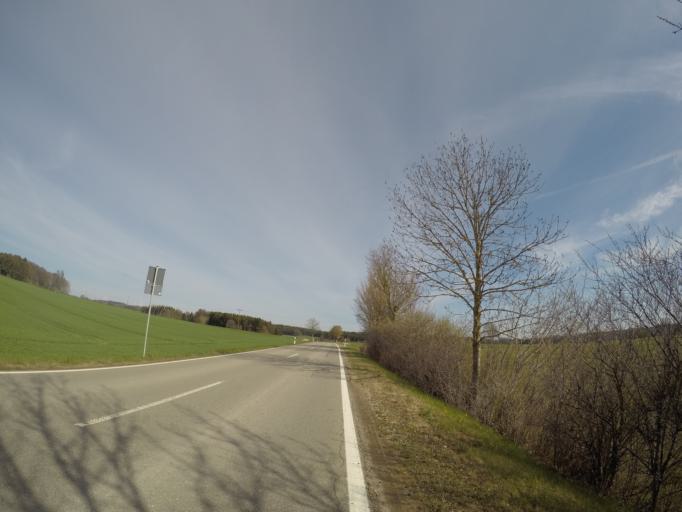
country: DE
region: Baden-Wuerttemberg
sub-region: Tuebingen Region
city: Laichingen
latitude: 48.5101
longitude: 9.6729
